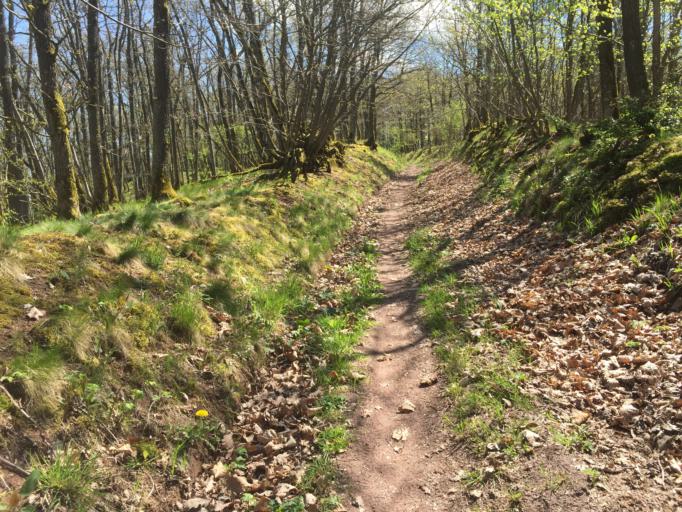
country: DE
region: Bavaria
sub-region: Regierungsbezirk Unterfranken
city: Sulzfeld
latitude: 50.2617
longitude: 10.4389
